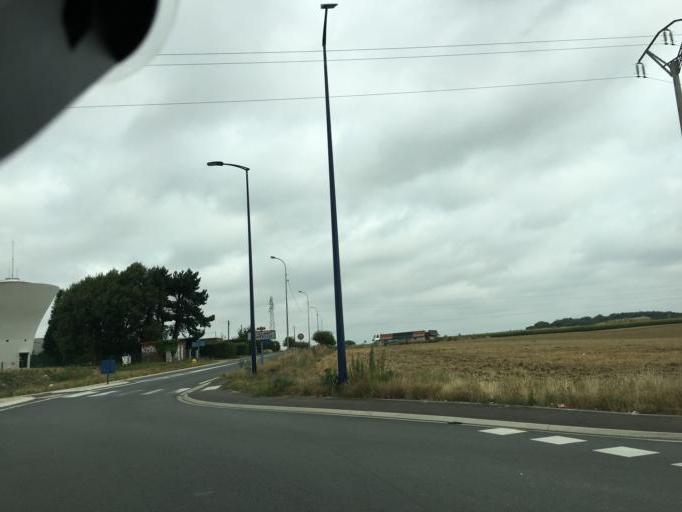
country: FR
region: Nord-Pas-de-Calais
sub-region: Departement du Pas-de-Calais
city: Saint-Pol-sur-Ternoise
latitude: 50.3877
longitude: 2.3501
